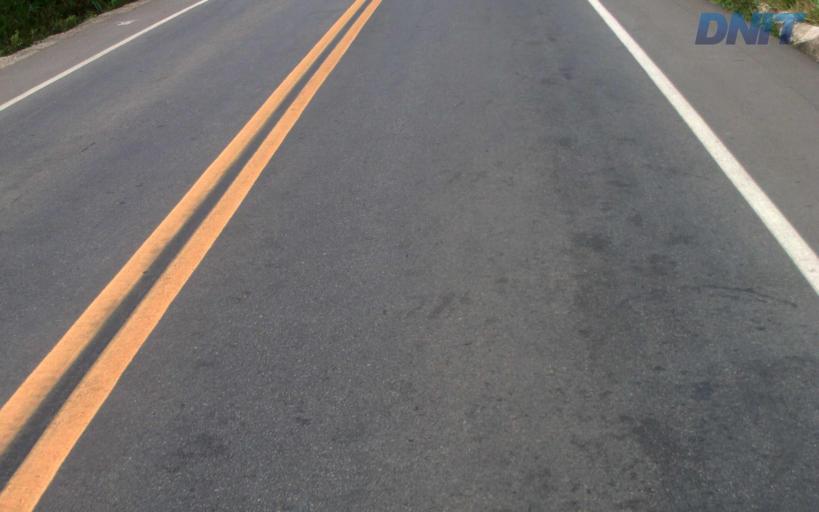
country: BR
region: Minas Gerais
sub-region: Belo Oriente
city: Belo Oriente
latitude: -19.2420
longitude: -42.3352
